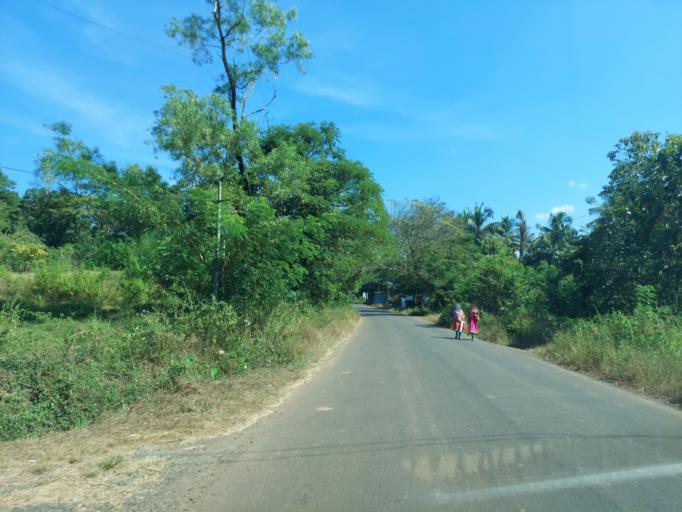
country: IN
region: Maharashtra
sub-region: Sindhudurg
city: Kudal
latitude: 15.9886
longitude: 73.6795
